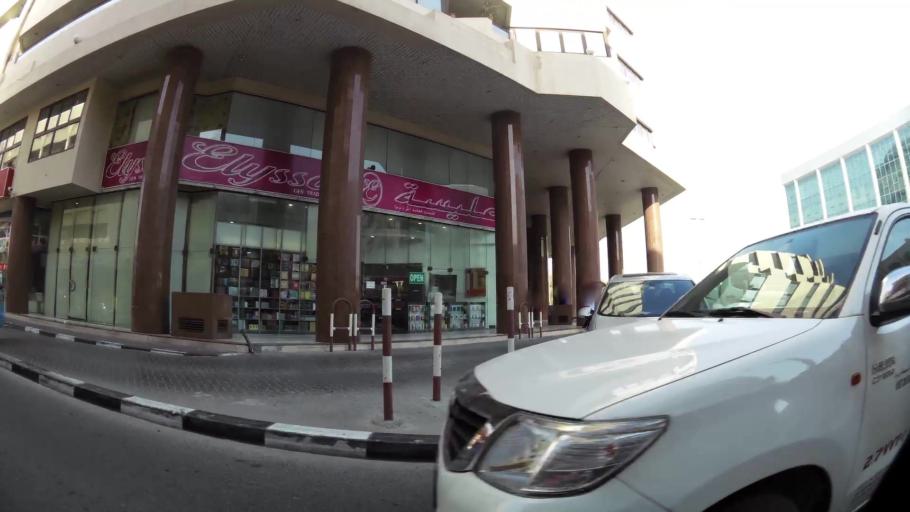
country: AE
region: Ash Shariqah
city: Sharjah
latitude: 25.2449
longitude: 55.3065
